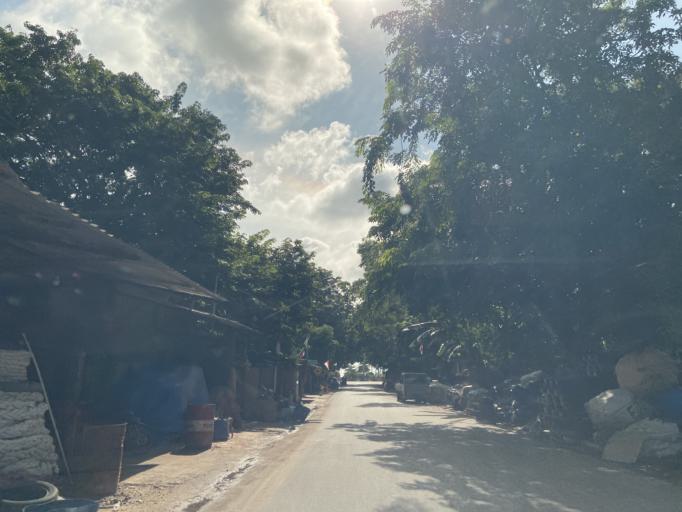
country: SG
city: Singapore
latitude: 1.1696
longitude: 104.0105
